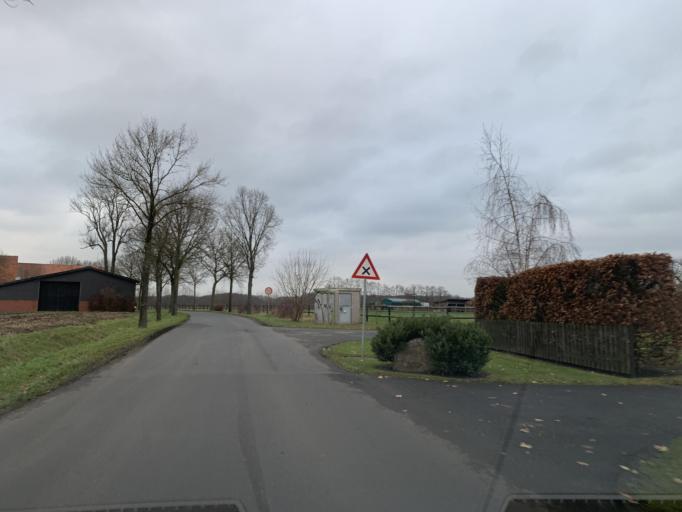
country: DE
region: North Rhine-Westphalia
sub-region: Regierungsbezirk Munster
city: Muenster
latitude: 51.9308
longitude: 7.5409
